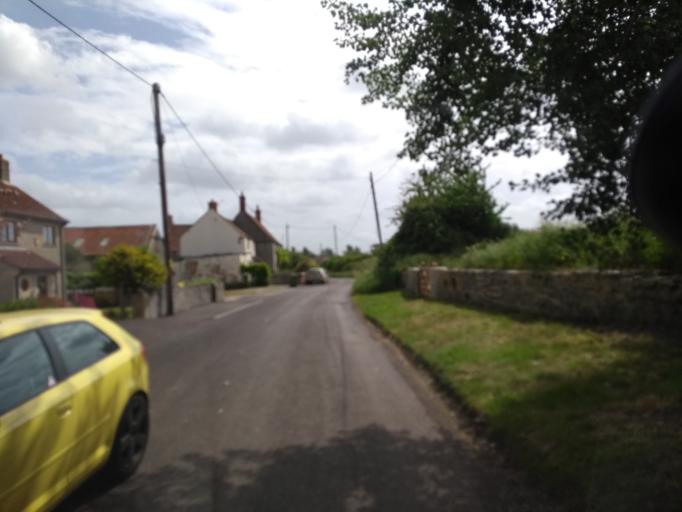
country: GB
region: England
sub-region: Somerset
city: Bridgwater
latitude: 51.1873
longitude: -3.0841
